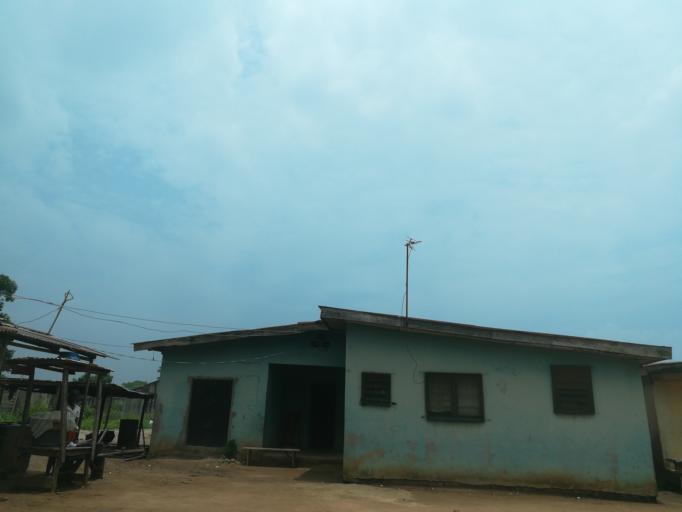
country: NG
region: Lagos
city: Ikorodu
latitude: 6.5699
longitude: 3.5932
